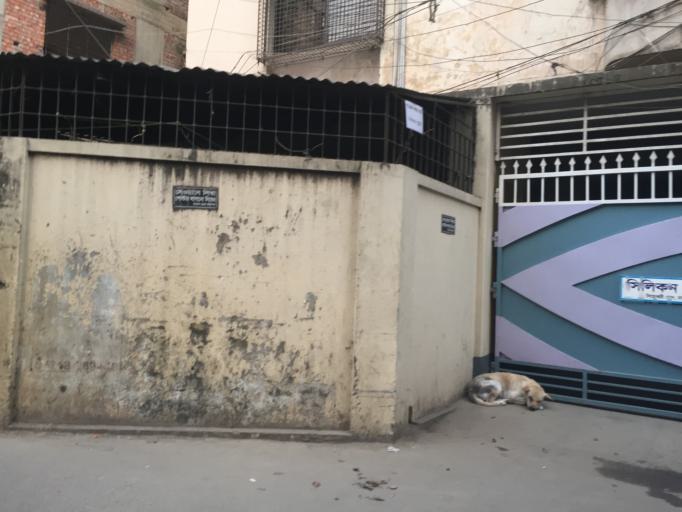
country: BD
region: Dhaka
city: Paltan
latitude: 23.7436
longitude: 90.4112
